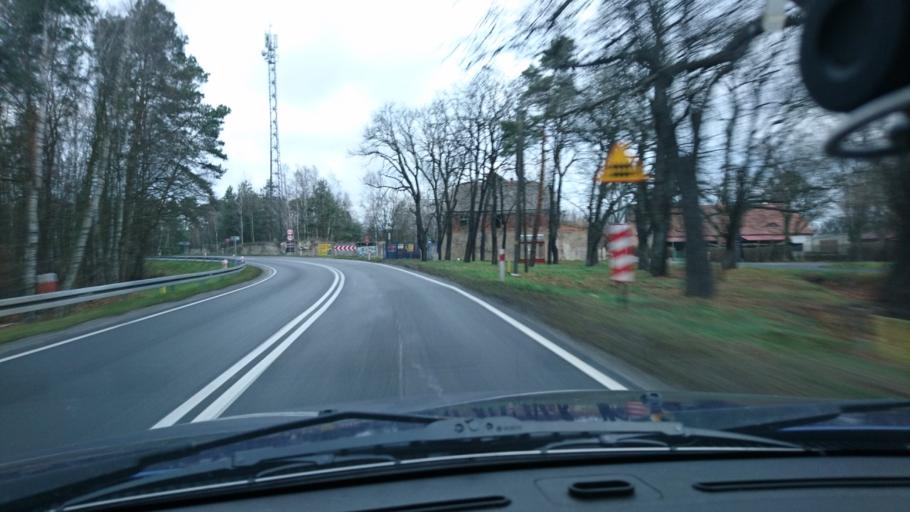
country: PL
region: Opole Voivodeship
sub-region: Powiat kluczborski
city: Kluczbork
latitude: 50.9559
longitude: 18.3089
